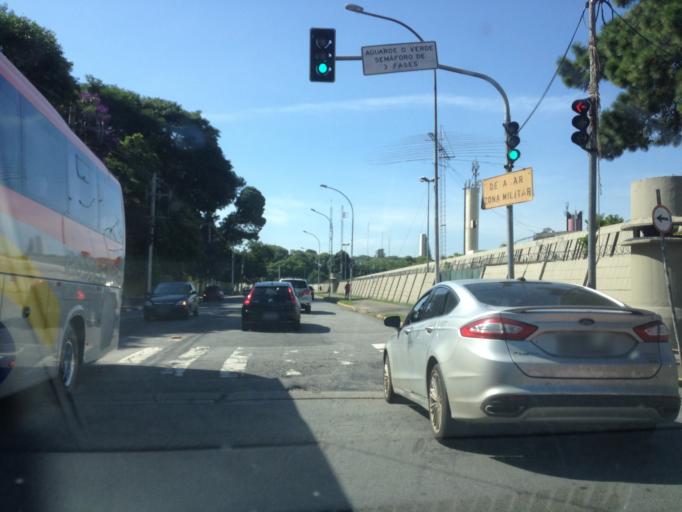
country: BR
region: Sao Paulo
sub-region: Sao Paulo
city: Sao Paulo
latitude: -23.5775
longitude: -46.6574
